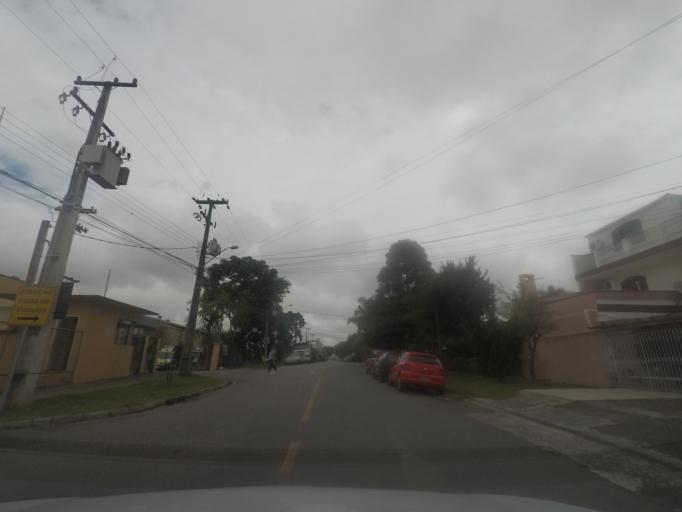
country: BR
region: Parana
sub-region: Pinhais
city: Pinhais
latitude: -25.4401
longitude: -49.2242
